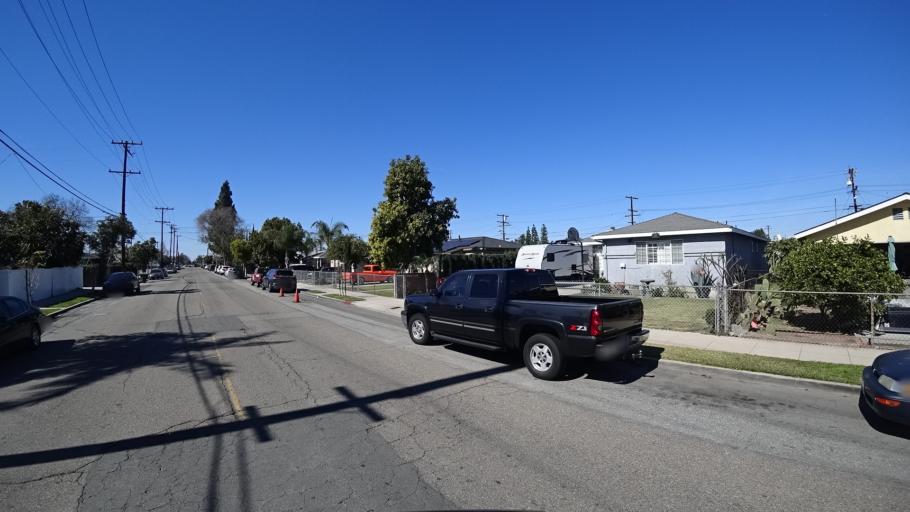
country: US
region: California
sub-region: Orange County
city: Anaheim
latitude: 33.8295
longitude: -117.9090
